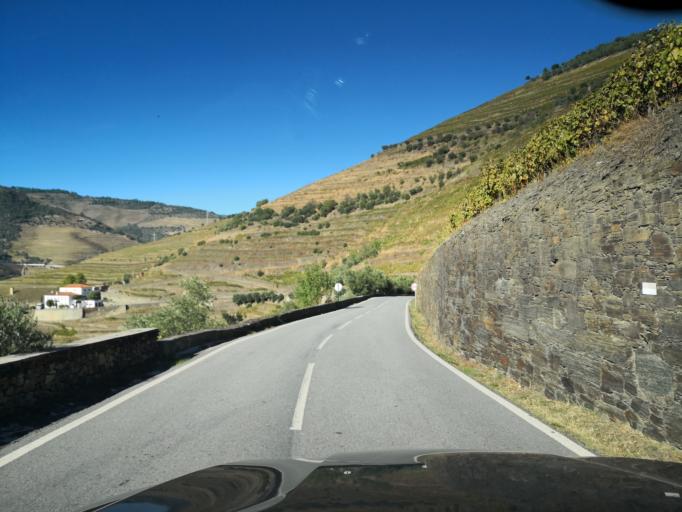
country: PT
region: Viseu
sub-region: Tabuaco
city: Tabuaco
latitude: 41.1693
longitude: -7.5470
